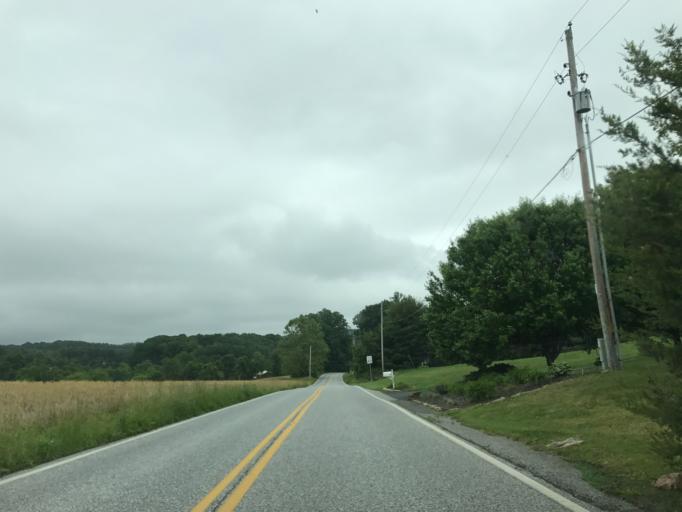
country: US
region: Pennsylvania
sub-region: York County
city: Susquehanna Trails
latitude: 39.7511
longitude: -76.4582
